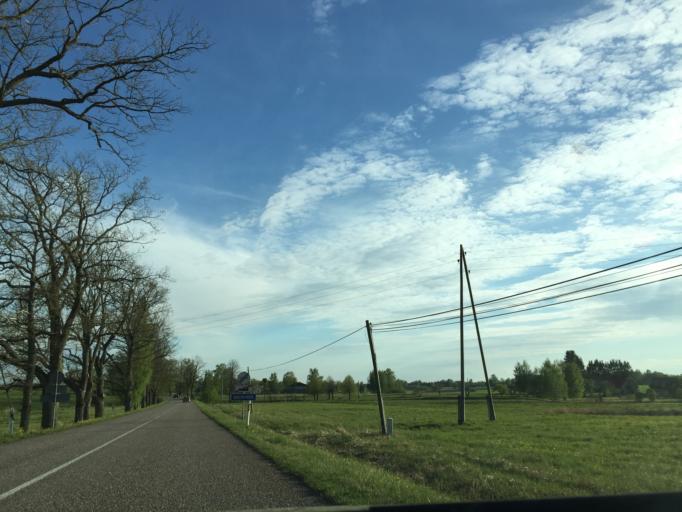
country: LV
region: Saulkrastu
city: Saulkrasti
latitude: 57.3695
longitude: 24.4921
